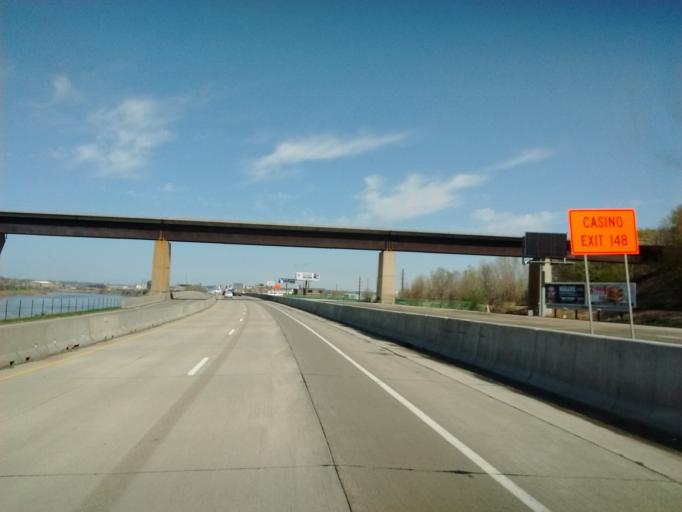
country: US
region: Nebraska
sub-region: Dakota County
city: South Sioux City
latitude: 42.4742
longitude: -96.3832
